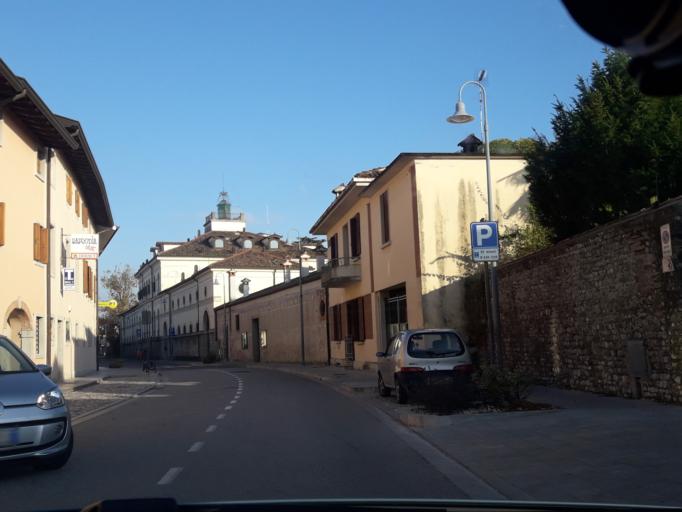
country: IT
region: Friuli Venezia Giulia
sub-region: Provincia di Udine
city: Pradamano
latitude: 46.0309
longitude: 13.2985
